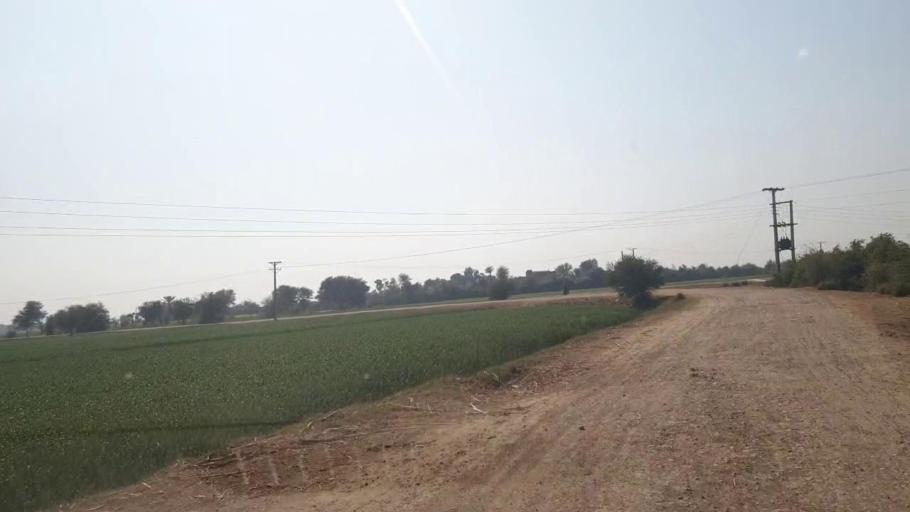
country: PK
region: Sindh
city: Shahdadpur
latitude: 26.0396
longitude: 68.4629
